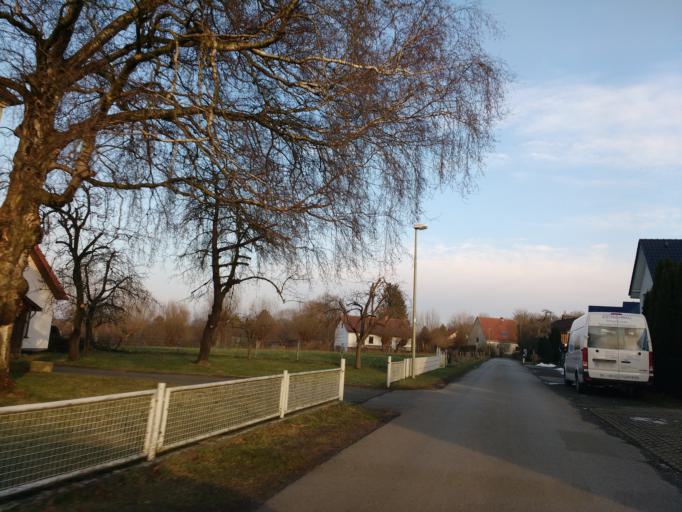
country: DE
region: North Rhine-Westphalia
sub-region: Regierungsbezirk Detmold
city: Paderborn
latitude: 51.7205
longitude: 8.6765
